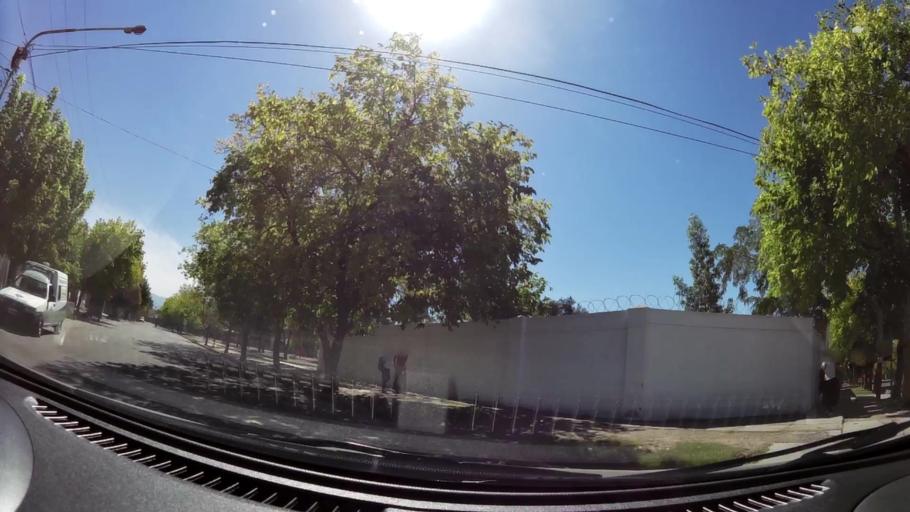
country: AR
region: Mendoza
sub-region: Departamento de Godoy Cruz
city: Godoy Cruz
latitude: -32.9661
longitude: -68.8325
